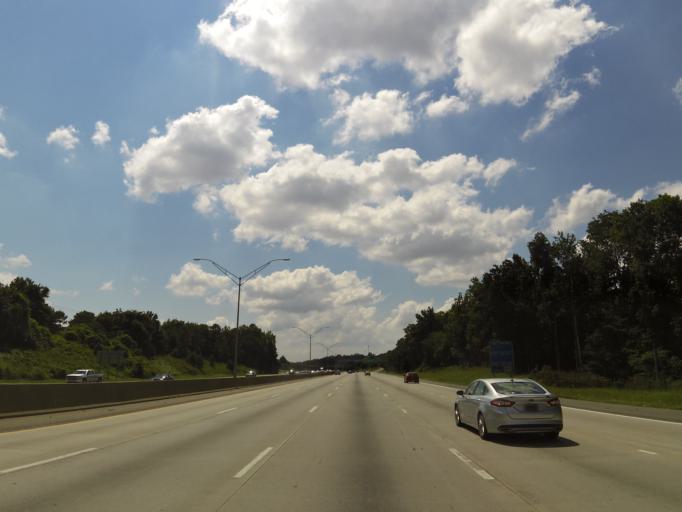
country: US
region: North Carolina
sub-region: Cabarrus County
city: Harrisburg
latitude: 35.3176
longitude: -80.7542
